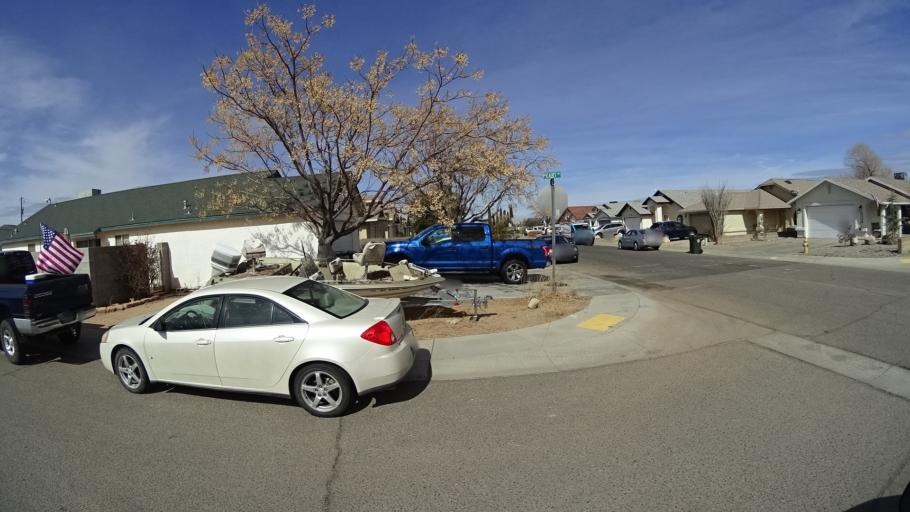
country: US
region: Arizona
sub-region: Mohave County
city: New Kingman-Butler
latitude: 35.2302
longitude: -114.0226
